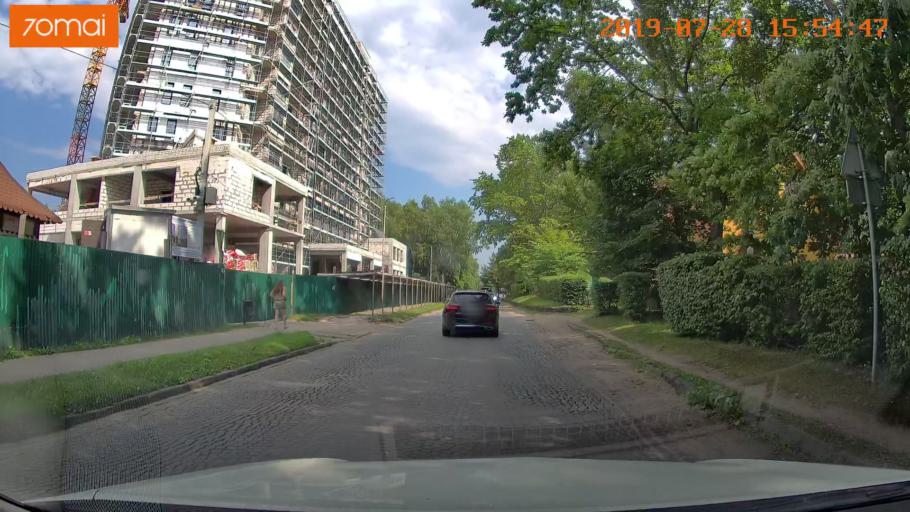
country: RU
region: Kaliningrad
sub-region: Gorod Svetlogorsk
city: Svetlogorsk
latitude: 54.9417
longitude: 20.1358
